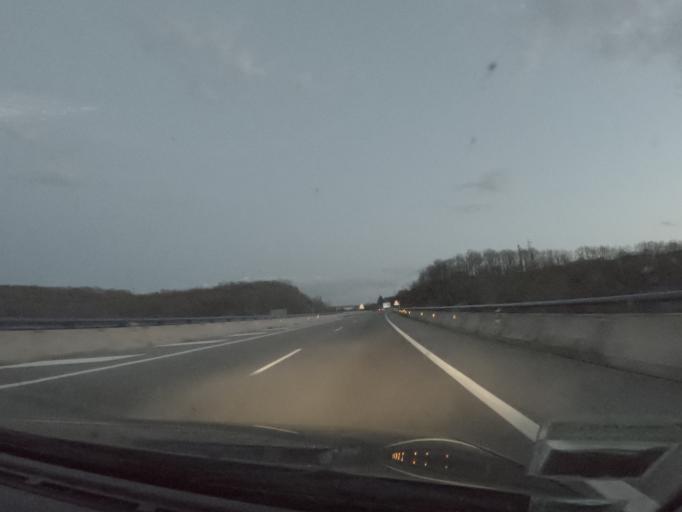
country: ES
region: Castille and Leon
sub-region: Provincia de Leon
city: Bembibre
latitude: 42.6196
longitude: -6.4063
